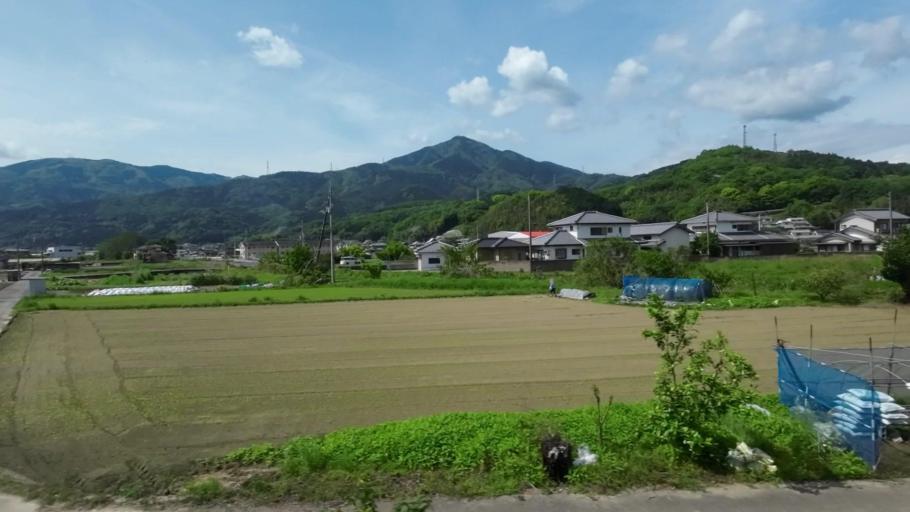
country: JP
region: Tokushima
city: Wakimachi
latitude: 34.0566
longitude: 134.2232
